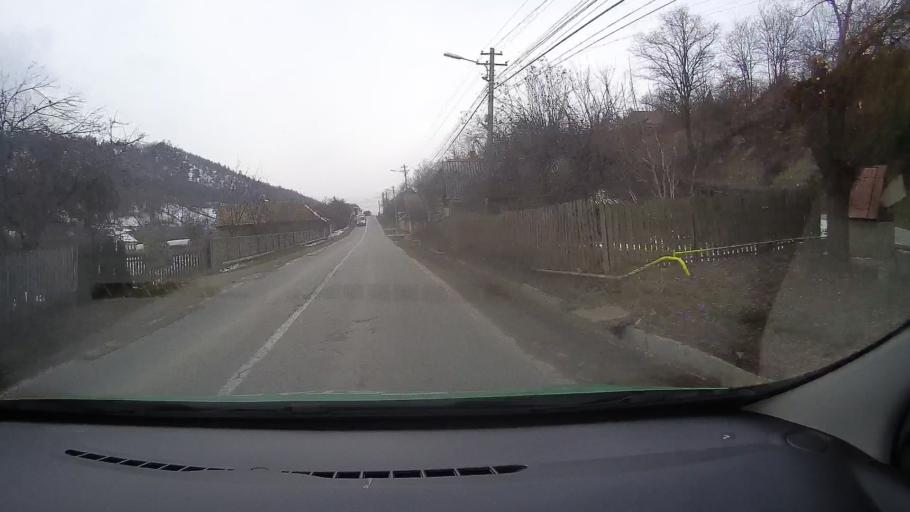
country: RO
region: Alba
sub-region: Oras Zlatna
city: Zlatna
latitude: 46.0918
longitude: 23.2584
